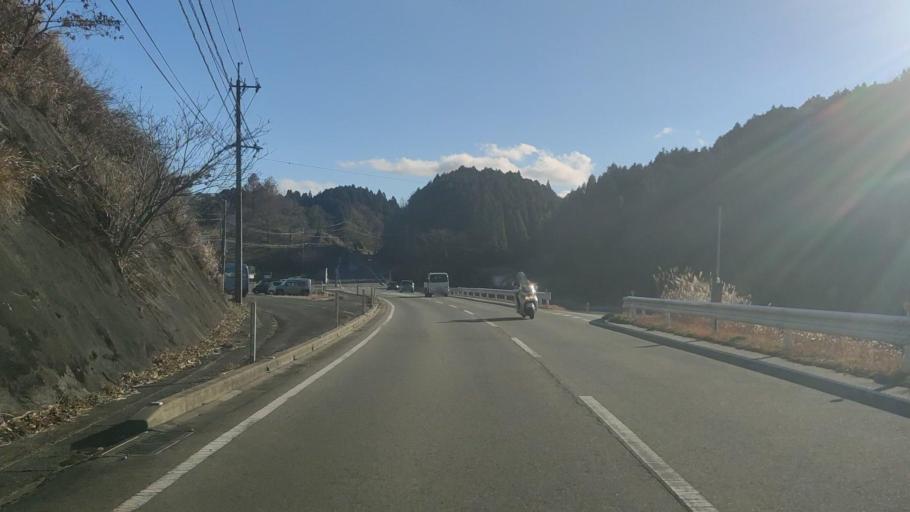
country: JP
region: Saga Prefecture
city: Kanzakimachi-kanzaki
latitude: 33.4075
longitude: 130.2722
